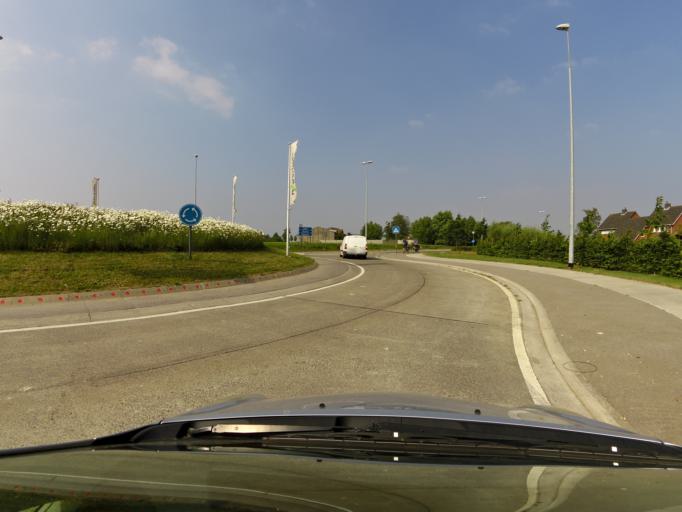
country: BE
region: Flanders
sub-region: Provincie West-Vlaanderen
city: Poperinge
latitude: 50.8641
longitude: 2.7179
